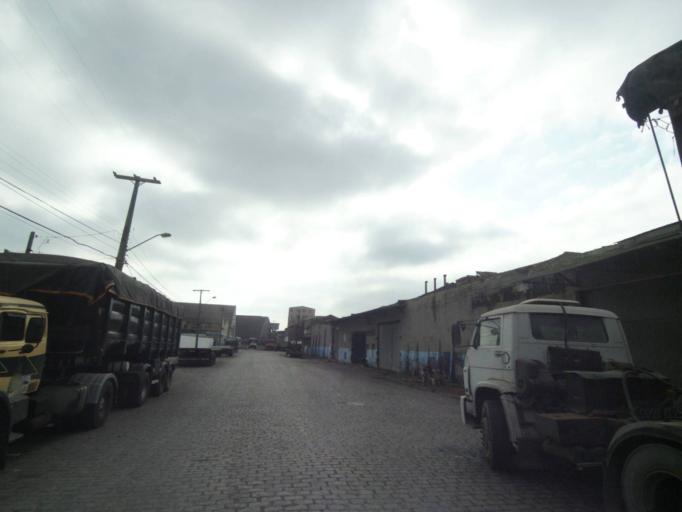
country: BR
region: Parana
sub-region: Paranagua
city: Paranagua
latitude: -25.5103
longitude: -48.5199
